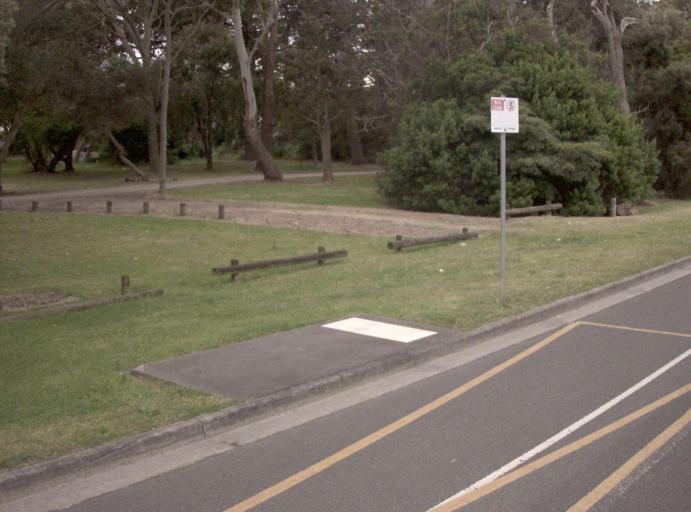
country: AU
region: Victoria
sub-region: Mornington Peninsula
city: Rosebud
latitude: -38.3589
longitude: 144.8933
